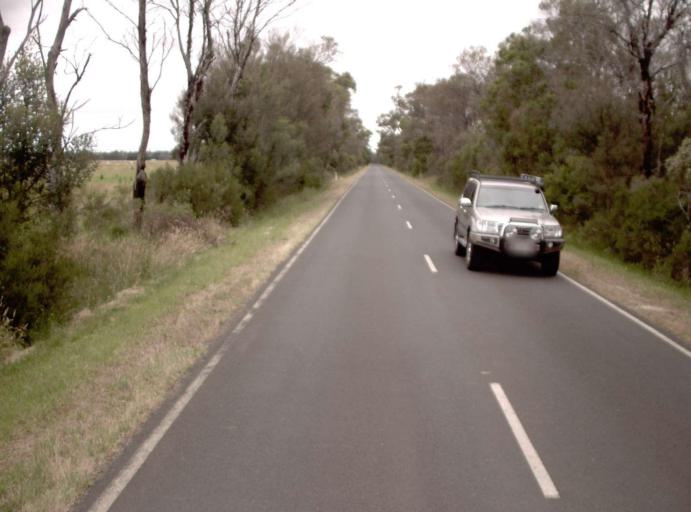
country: AU
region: Victoria
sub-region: Latrobe
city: Traralgon
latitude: -38.4828
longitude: 146.8207
